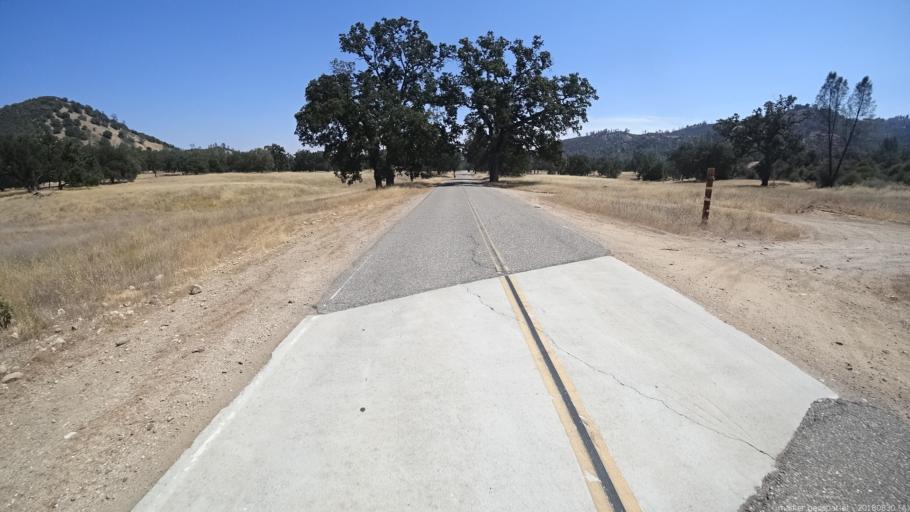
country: US
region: California
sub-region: Monterey County
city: King City
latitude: 36.0120
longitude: -121.2808
